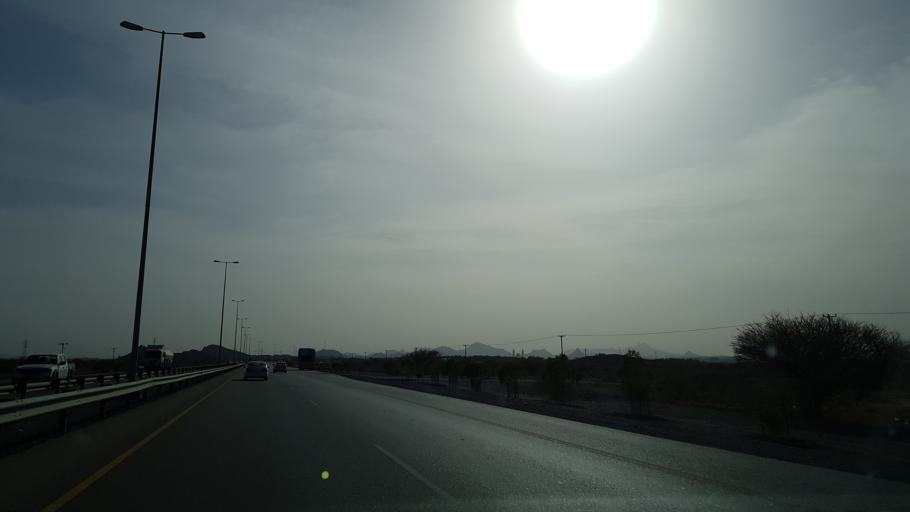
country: OM
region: Muhafazat ad Dakhiliyah
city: Nizwa
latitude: 22.8608
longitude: 57.5758
